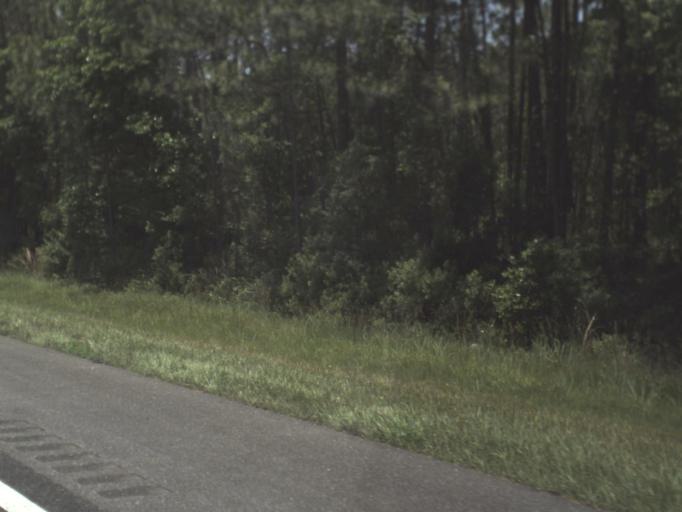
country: US
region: Florida
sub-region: Columbia County
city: Watertown
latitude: 30.2550
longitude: -82.4361
